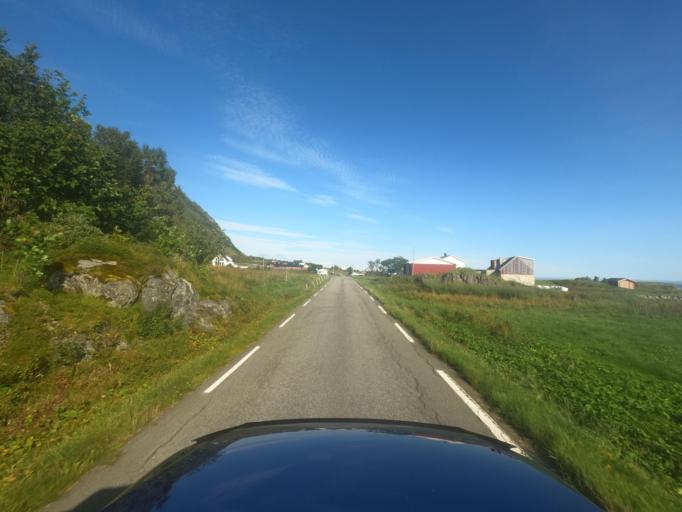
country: NO
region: Nordland
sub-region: Vestvagoy
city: Evjen
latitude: 68.3163
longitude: 14.0142
